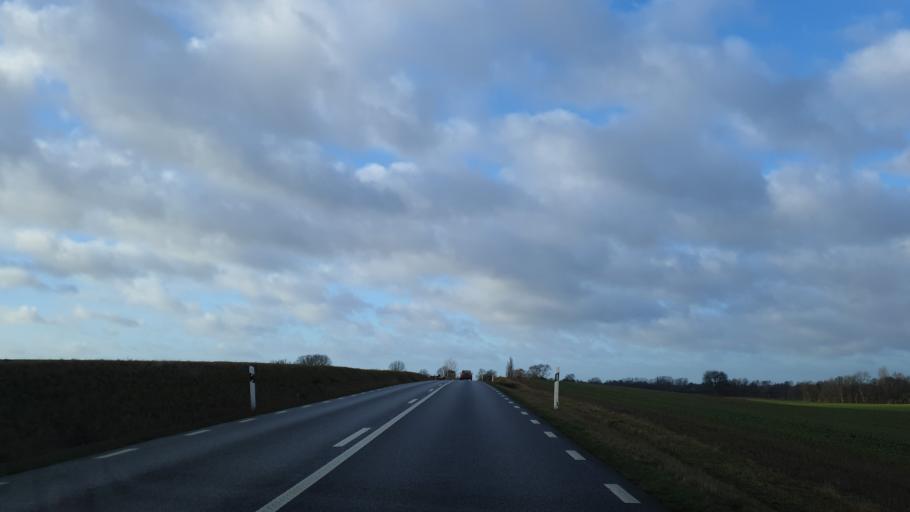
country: SE
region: Skane
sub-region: Trelleborgs Kommun
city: Trelleborg
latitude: 55.4593
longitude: 13.1601
